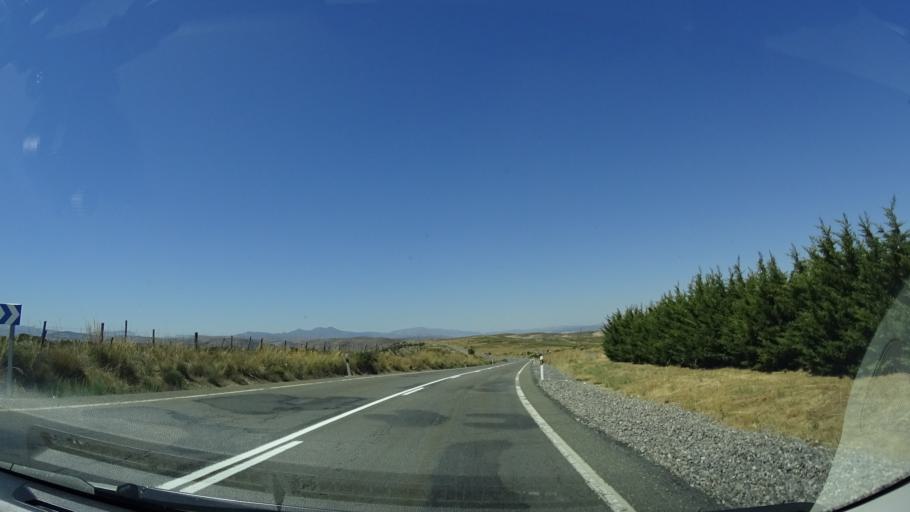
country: ES
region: Castille and Leon
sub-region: Provincia de Avila
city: Santa Cruz de Pinares
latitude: 40.6109
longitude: -4.5243
